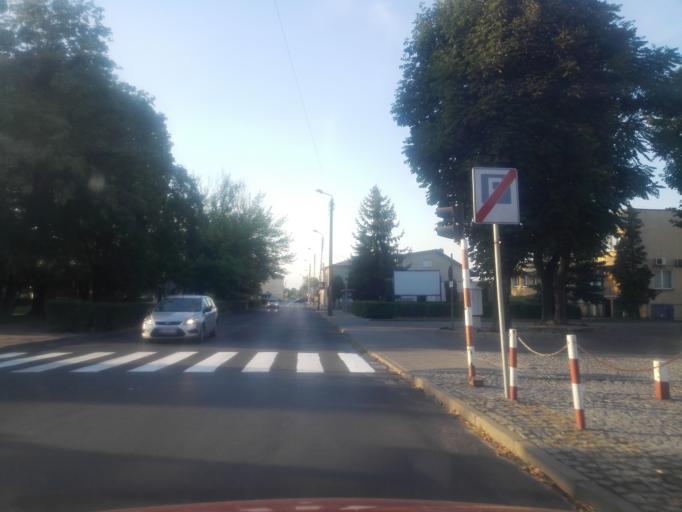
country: PL
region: Lodz Voivodeship
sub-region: Powiat wielunski
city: Wielun
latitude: 51.2202
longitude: 18.5741
